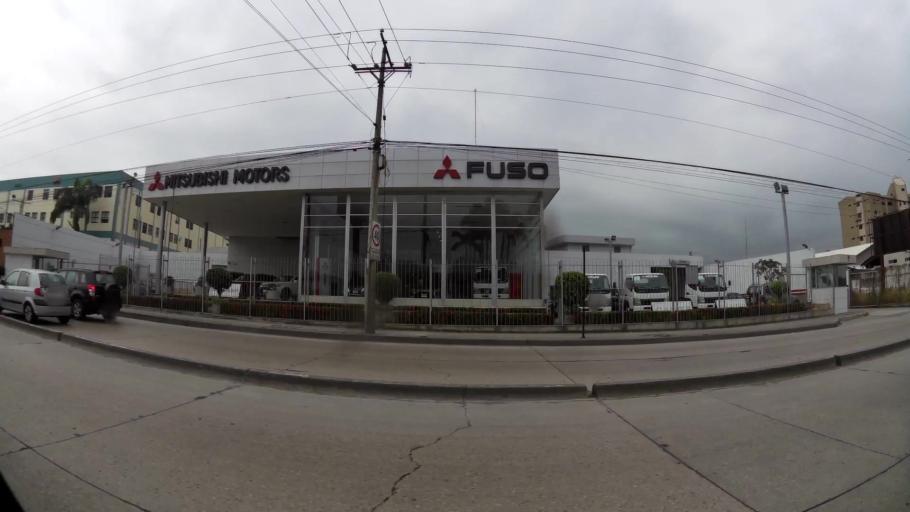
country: EC
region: Guayas
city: Eloy Alfaro
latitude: -2.1509
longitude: -79.8989
